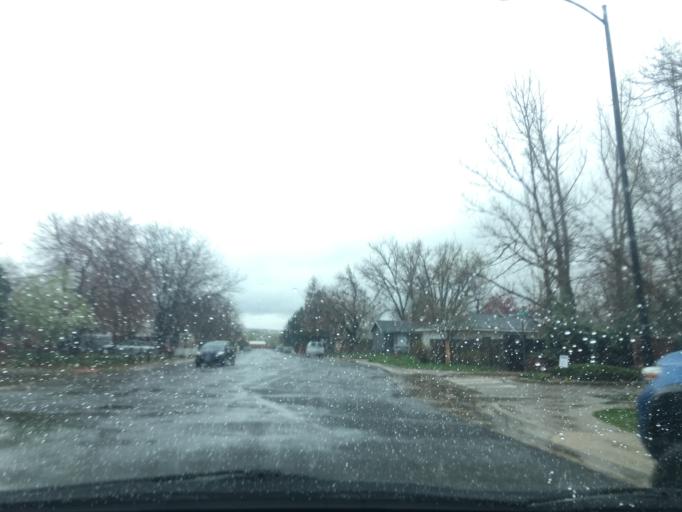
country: US
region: Colorado
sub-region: Boulder County
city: Lafayette
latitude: 39.9835
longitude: -105.0820
